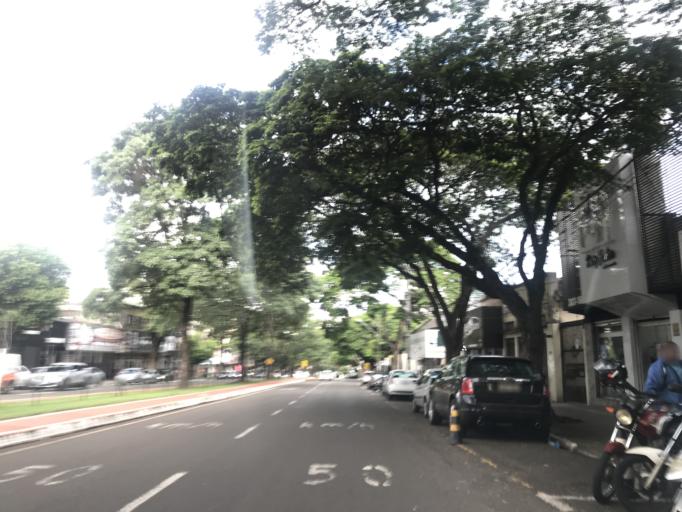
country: BR
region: Parana
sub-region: Maringa
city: Maringa
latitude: -23.4226
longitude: -51.9525
